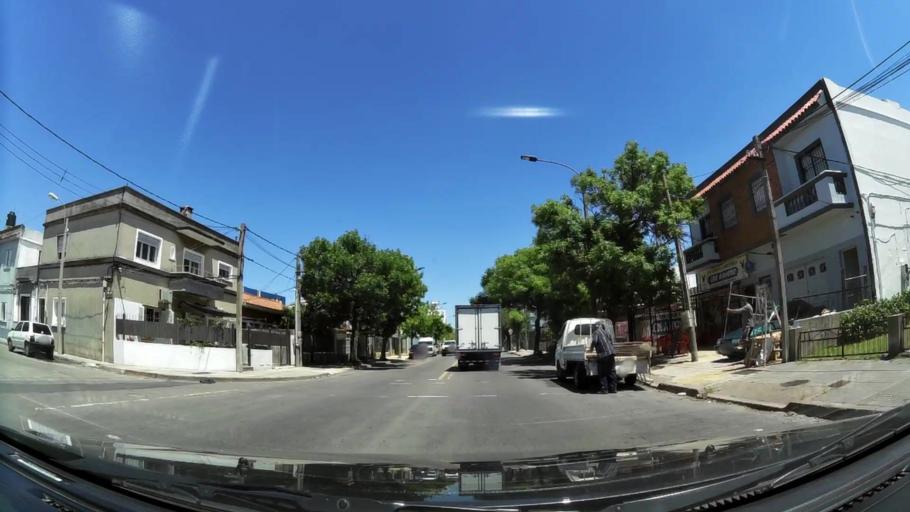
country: UY
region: Montevideo
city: Montevideo
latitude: -34.8946
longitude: -56.1398
